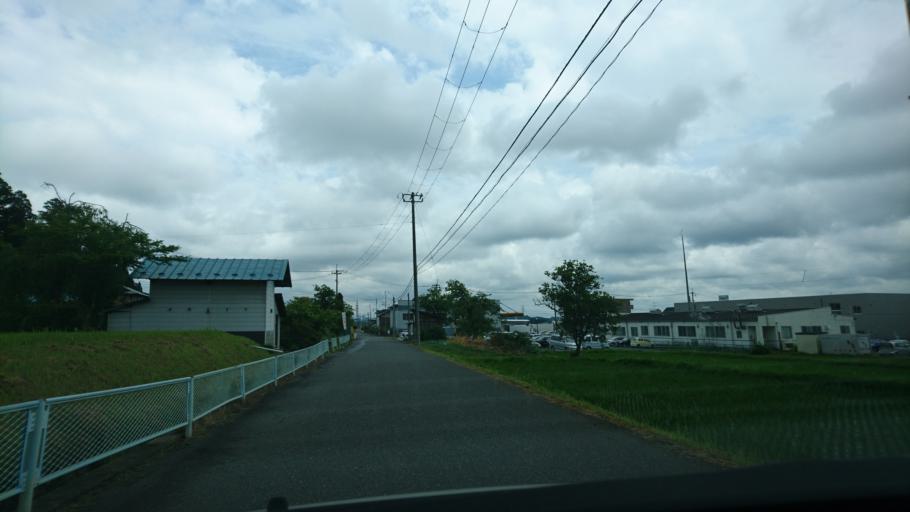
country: JP
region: Iwate
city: Ichinoseki
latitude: 38.9427
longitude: 141.0918
